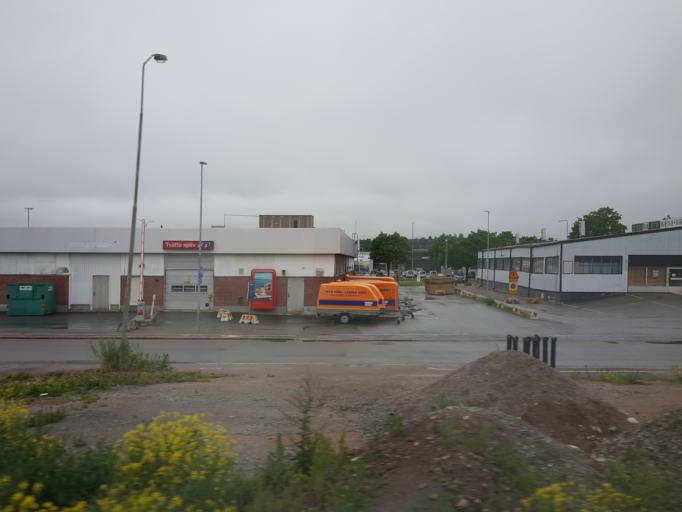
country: SE
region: Uppsala
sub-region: Uppsala Kommun
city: Uppsala
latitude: 59.8486
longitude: 17.6653
